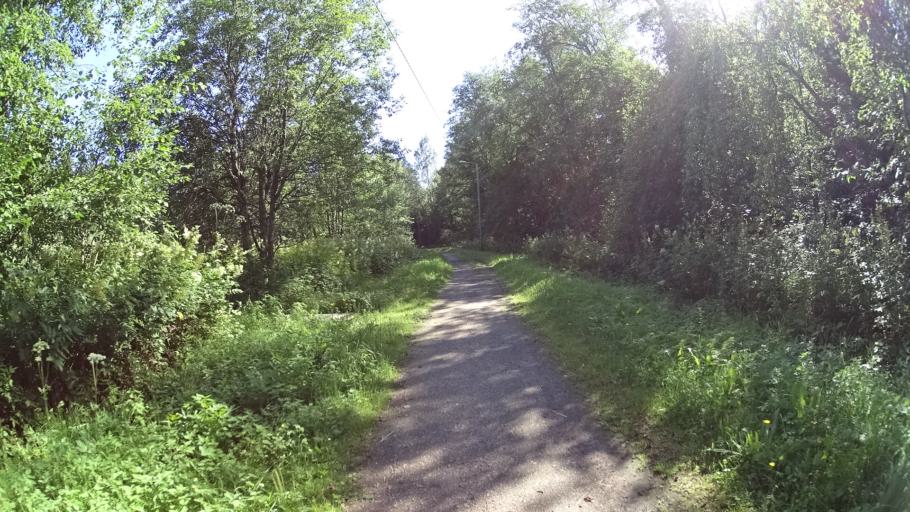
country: FI
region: Uusimaa
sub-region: Helsinki
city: Espoo
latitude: 60.2262
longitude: 24.6614
